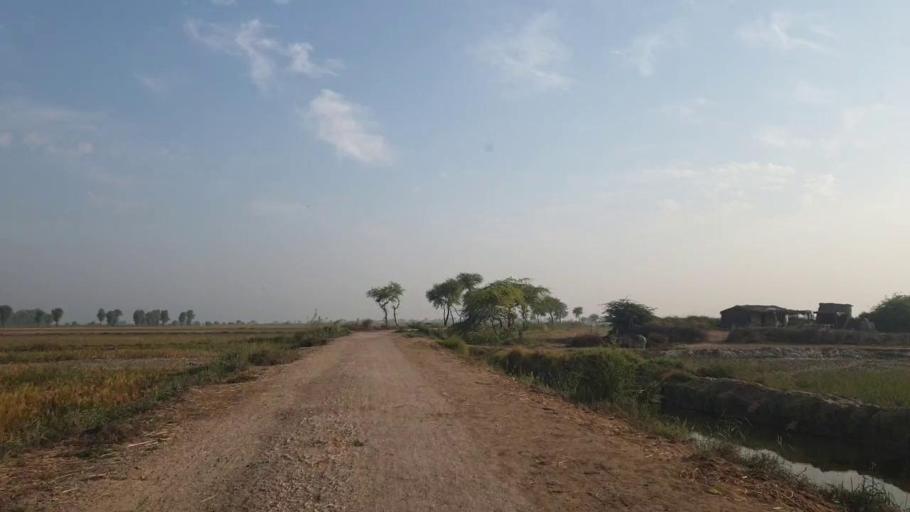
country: PK
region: Sindh
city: Tando Bago
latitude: 24.8202
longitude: 68.9577
